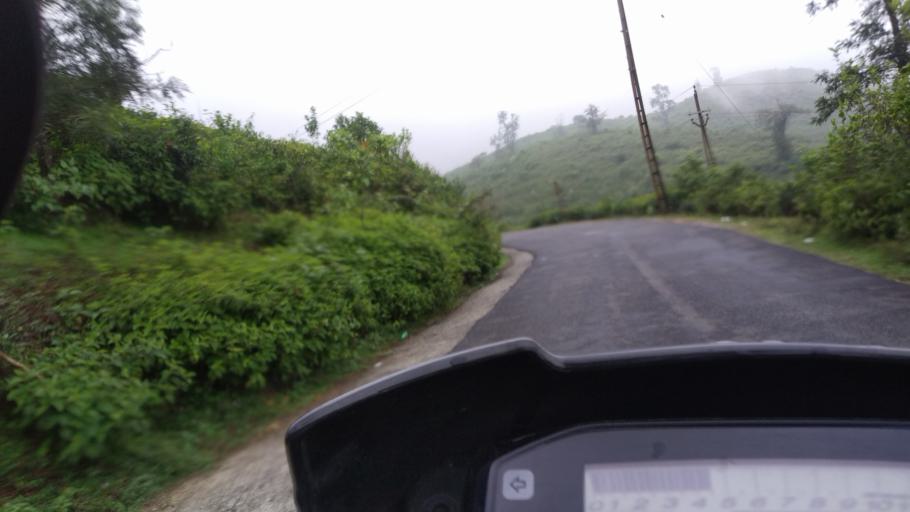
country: IN
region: Kerala
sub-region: Kottayam
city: Erattupetta
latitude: 9.6353
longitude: 76.9346
